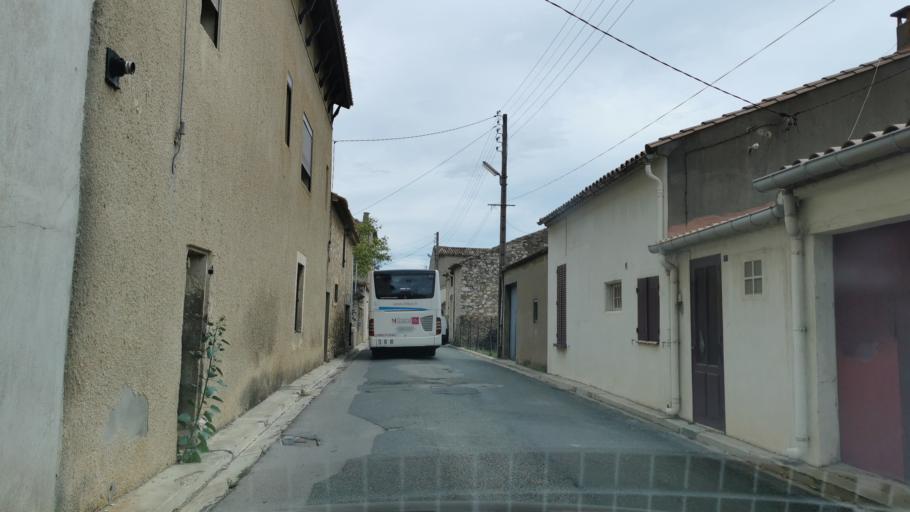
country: FR
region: Languedoc-Roussillon
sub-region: Departement de l'Aude
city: Argeliers
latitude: 43.3107
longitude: 2.9098
